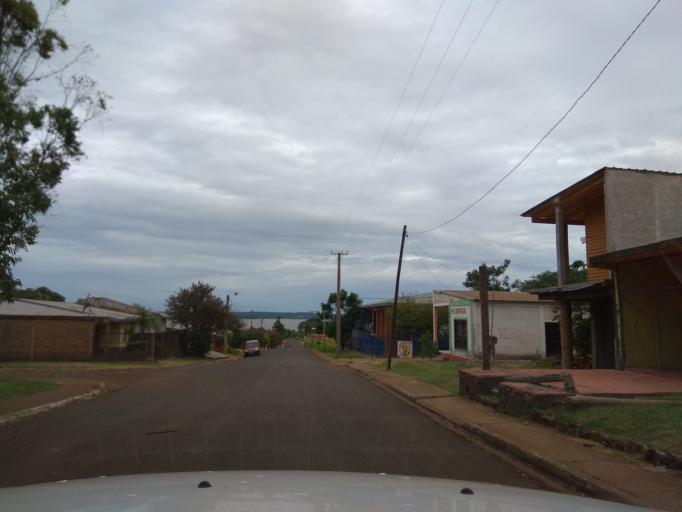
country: AR
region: Misiones
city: Garupa
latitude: -27.4499
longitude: -55.8565
